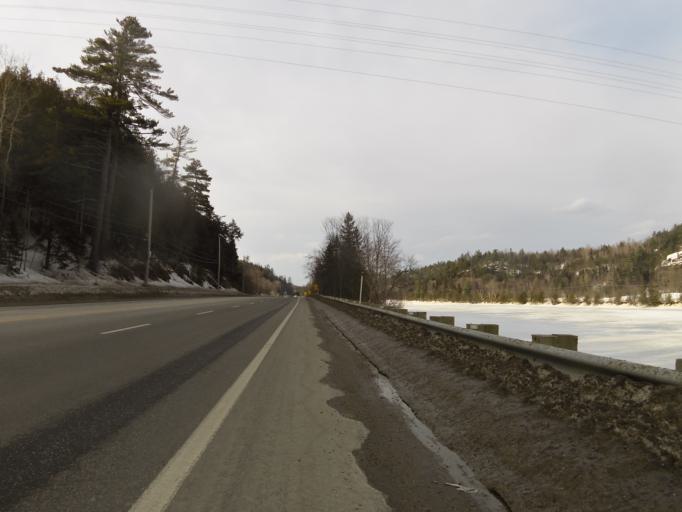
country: CA
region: Quebec
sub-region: Outaouais
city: Wakefield
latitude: 45.6678
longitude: -75.9281
